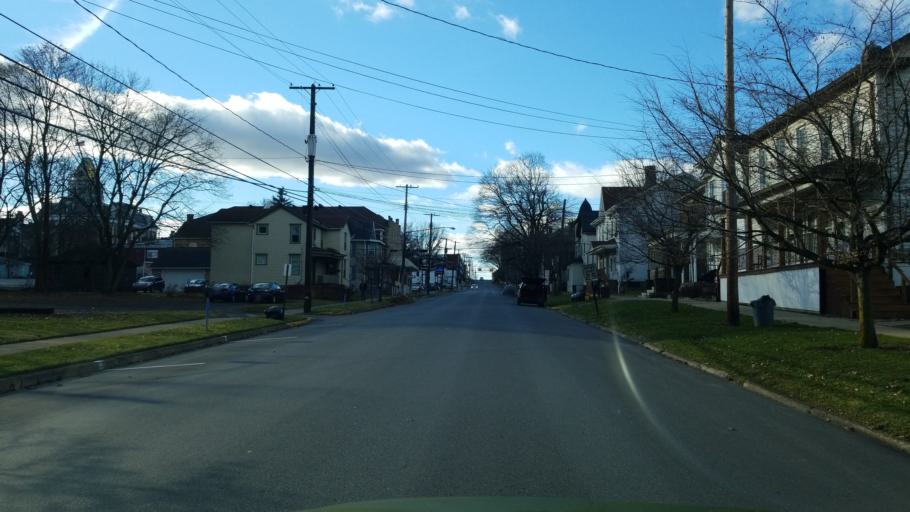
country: US
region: Pennsylvania
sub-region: Indiana County
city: Indiana
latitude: 40.6243
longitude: -79.1486
